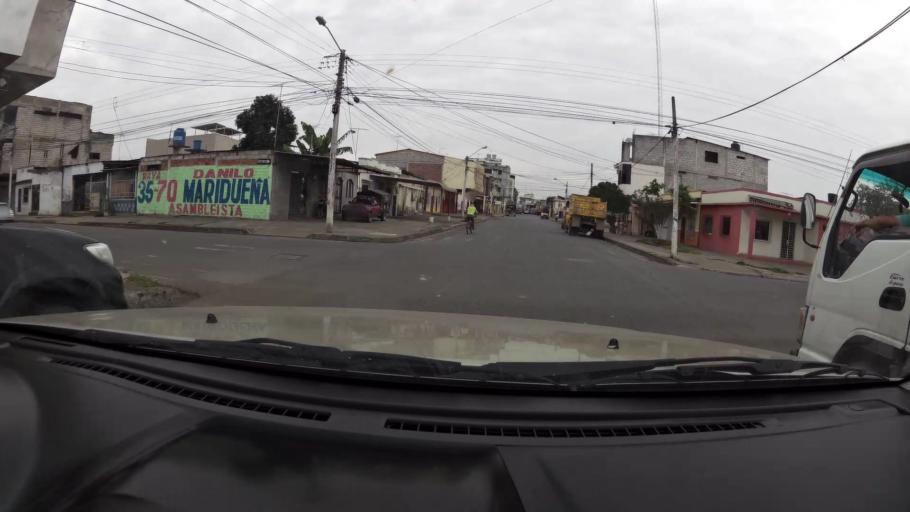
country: EC
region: El Oro
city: Machala
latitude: -3.2617
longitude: -79.9507
